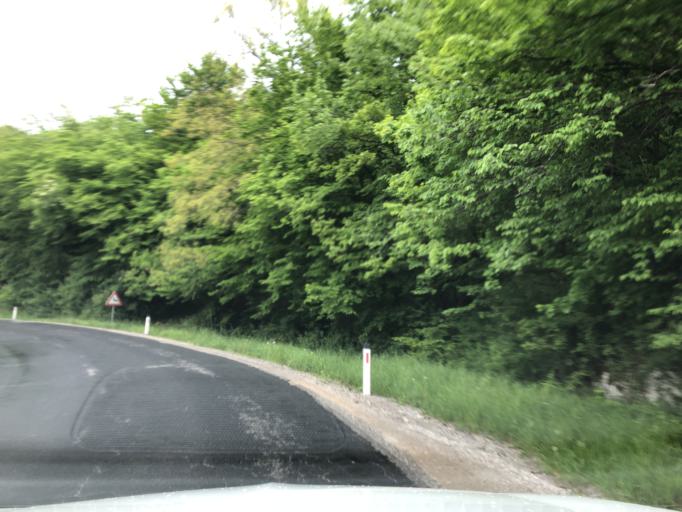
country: SI
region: Bloke
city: Nova Vas
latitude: 45.7639
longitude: 14.4323
